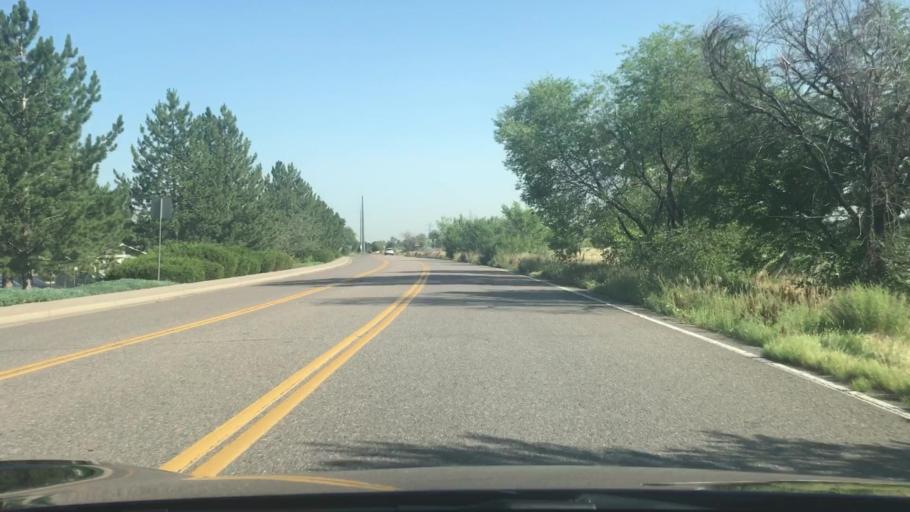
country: US
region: Colorado
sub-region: Arapahoe County
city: Glendale
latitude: 39.6759
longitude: -104.8946
